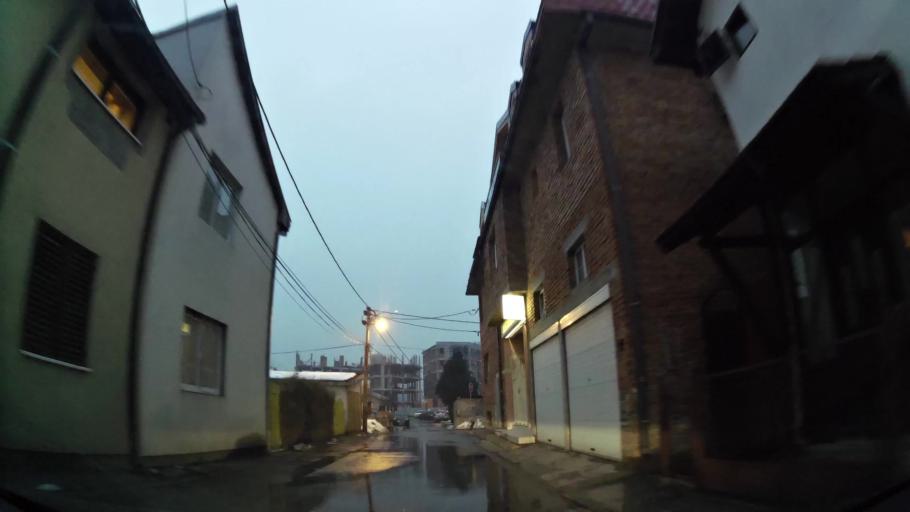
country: RS
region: Central Serbia
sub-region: Belgrade
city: Vozdovac
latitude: 44.7806
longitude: 20.4810
